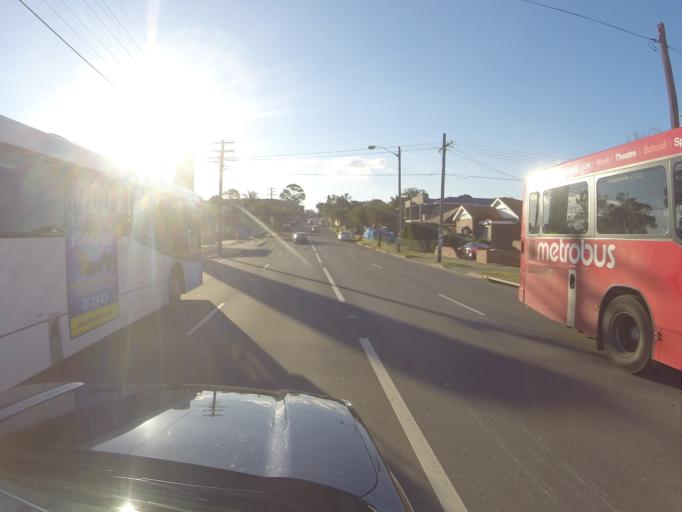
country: AU
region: New South Wales
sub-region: Canterbury
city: Canterbury
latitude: -33.9229
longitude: 151.1073
